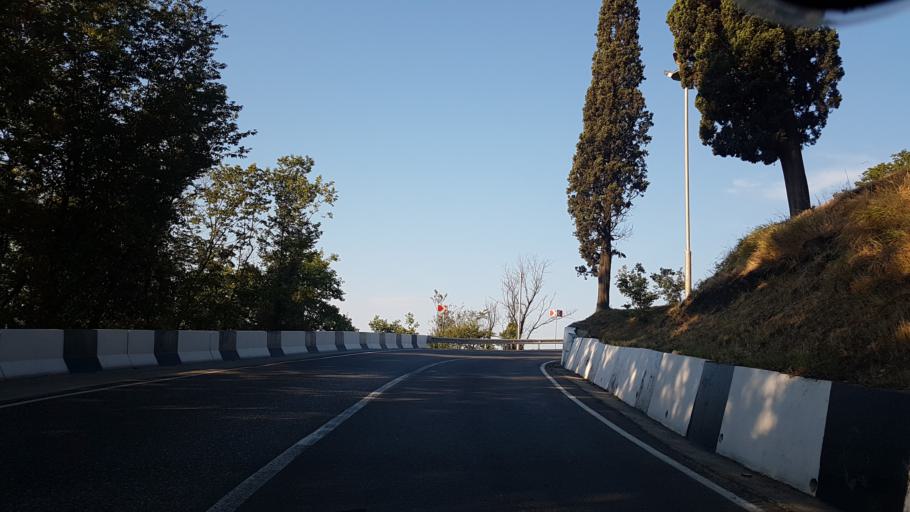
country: RU
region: Krasnodarskiy
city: Dagomys
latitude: 43.6554
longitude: 39.6454
